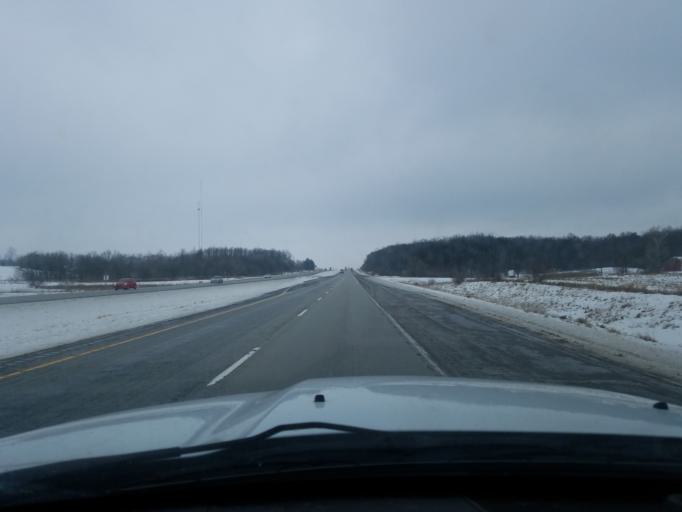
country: US
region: Indiana
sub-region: Fulton County
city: Rochester
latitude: 41.1087
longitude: -86.2397
